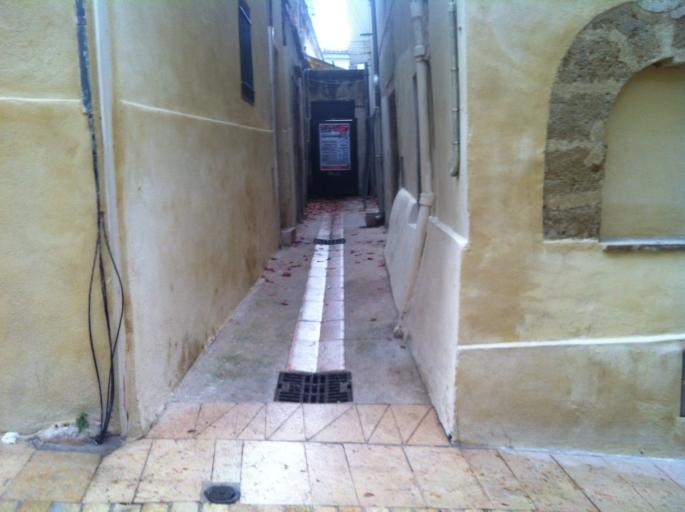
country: FR
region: Languedoc-Roussillon
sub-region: Departement de l'Herault
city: Montpellier
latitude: 43.6134
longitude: 3.8777
